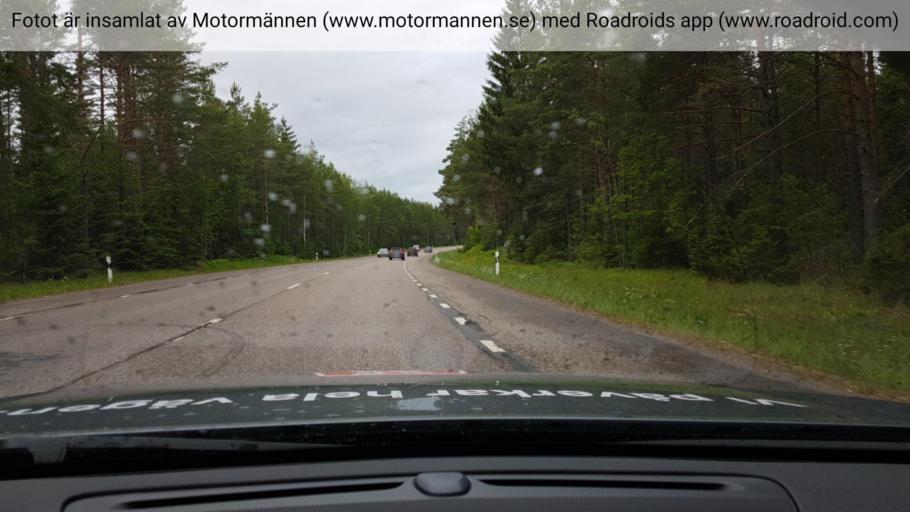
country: SE
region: Uppsala
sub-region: Alvkarleby Kommun
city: AElvkarleby
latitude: 60.6056
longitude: 17.4396
